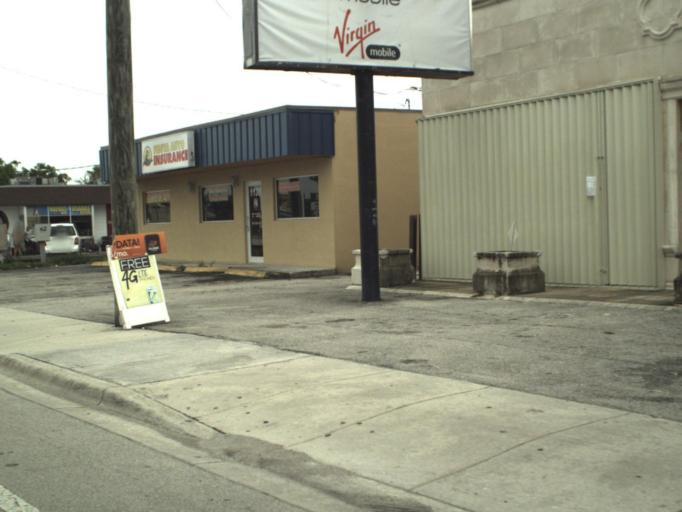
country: US
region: Florida
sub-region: Palm Beach County
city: Royal Palm Estates
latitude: 26.6603
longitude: -80.1125
